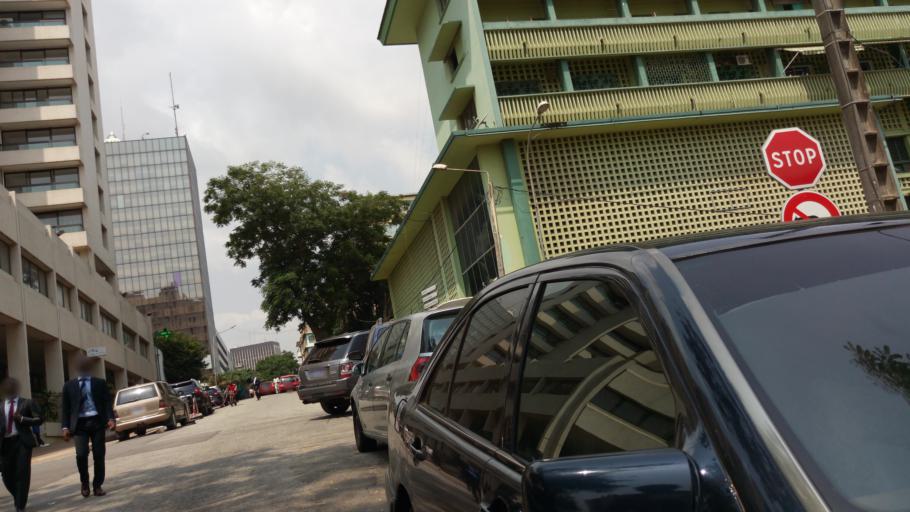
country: CI
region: Lagunes
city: Abidjan
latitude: 5.3193
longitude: -4.0164
